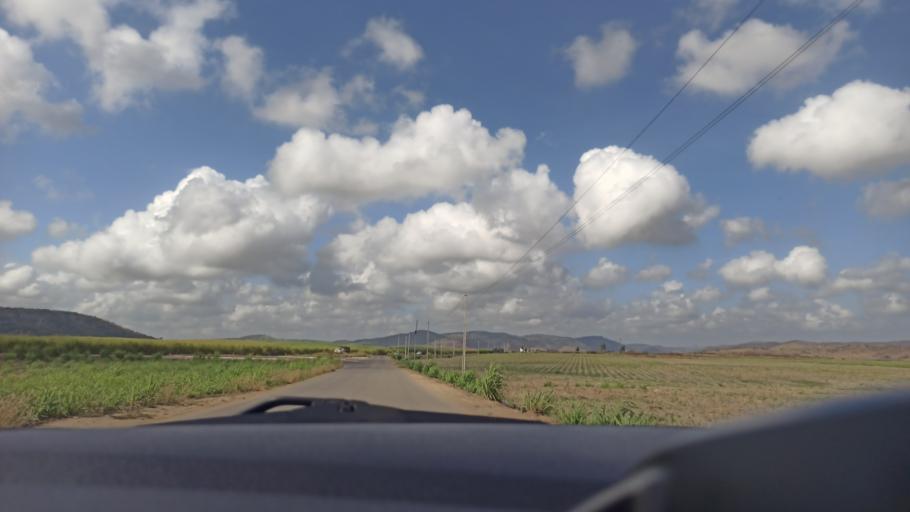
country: BR
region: Paraiba
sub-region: Juripiranga
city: Juripiranga
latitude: -7.3830
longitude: -35.2469
